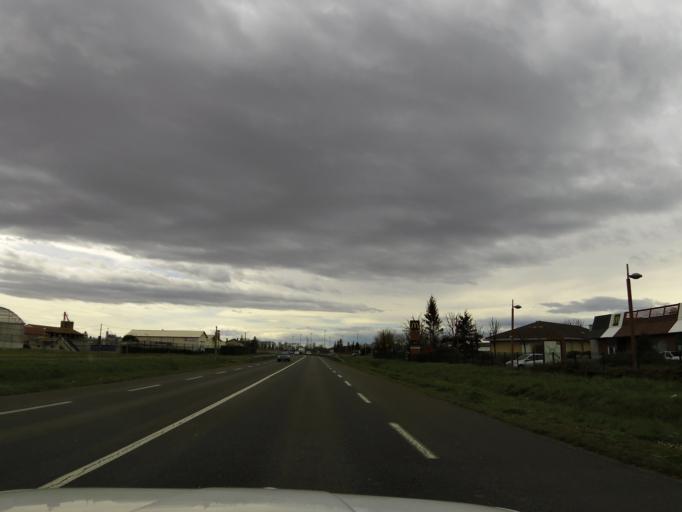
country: FR
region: Rhone-Alpes
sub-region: Departement de l'Ain
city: Meximieux
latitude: 45.9009
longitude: 5.1971
